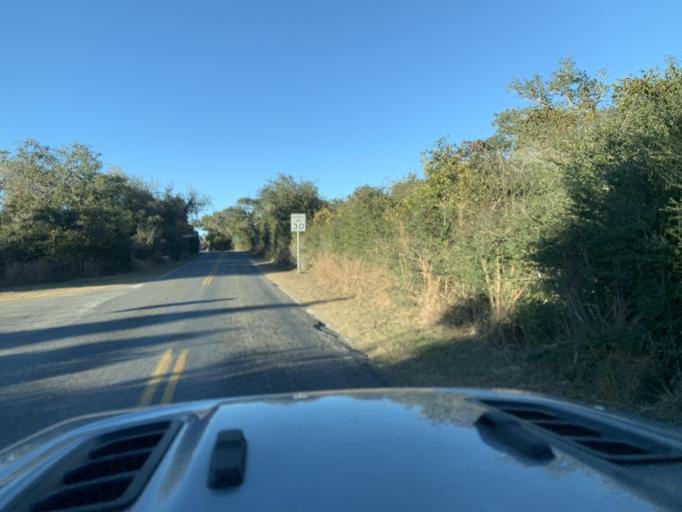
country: US
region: Texas
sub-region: Aransas County
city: Fulton
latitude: 28.1391
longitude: -96.9842
